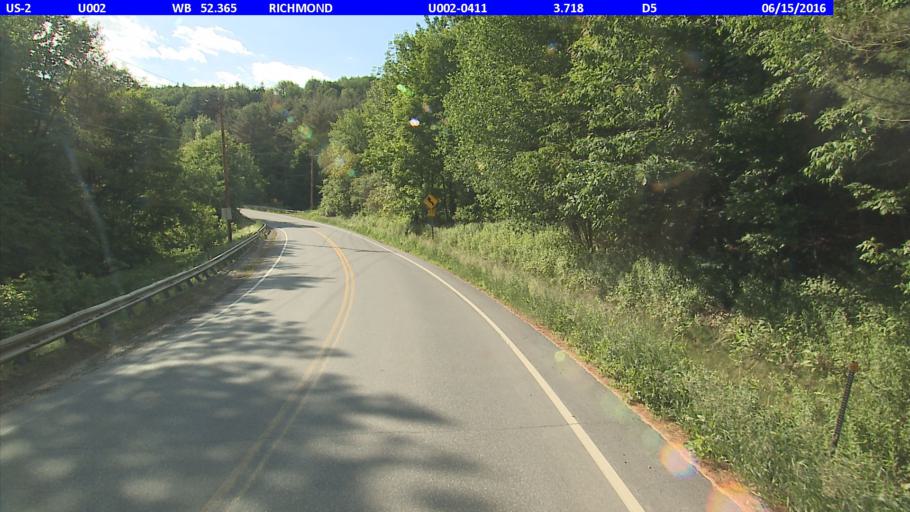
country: US
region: Vermont
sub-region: Chittenden County
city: Williston
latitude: 44.4024
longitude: -72.9764
